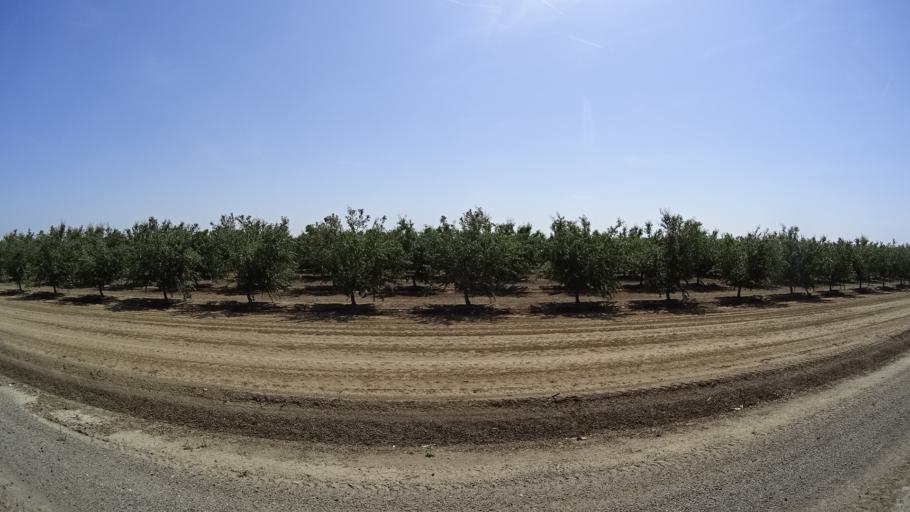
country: US
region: California
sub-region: Kings County
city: Kettleman City
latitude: 36.0895
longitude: -120.0037
